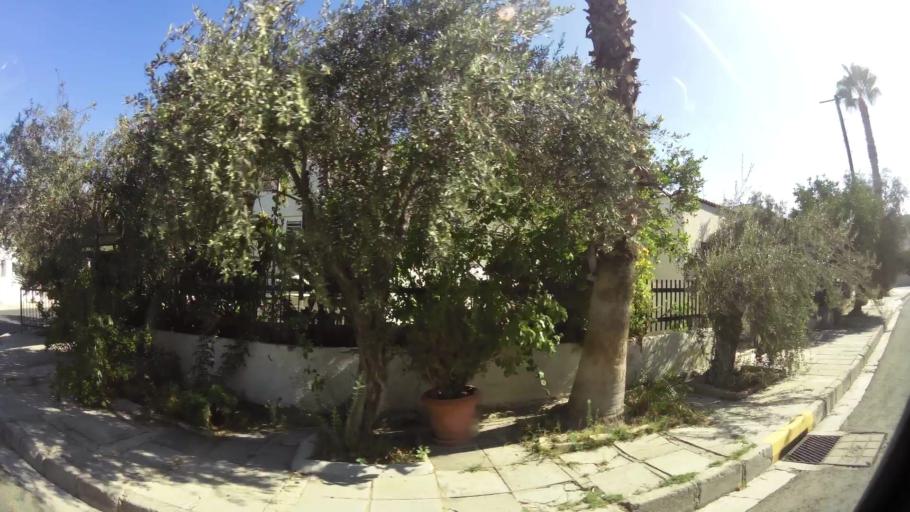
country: CY
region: Lefkosia
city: Nicosia
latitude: 35.1378
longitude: 33.3450
